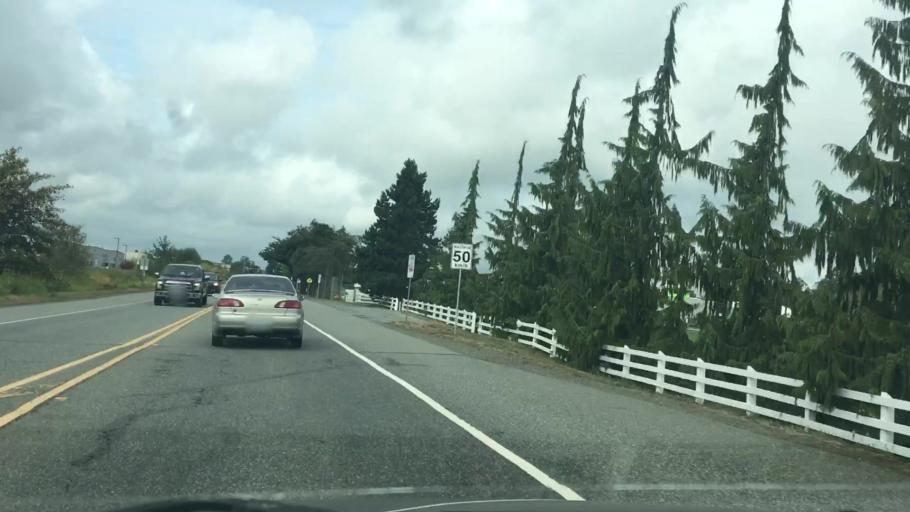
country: CA
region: British Columbia
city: Langley
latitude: 49.1044
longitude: -122.6260
